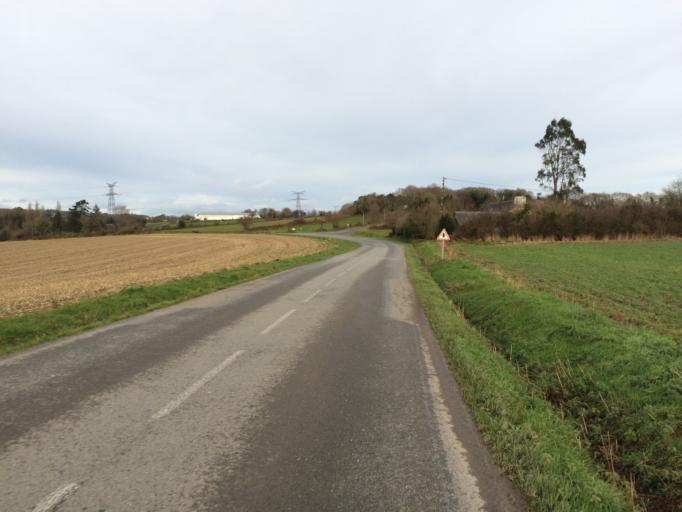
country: FR
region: Brittany
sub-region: Departement du Finistere
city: Saint-Urbain
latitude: 48.3836
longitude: -4.2378
